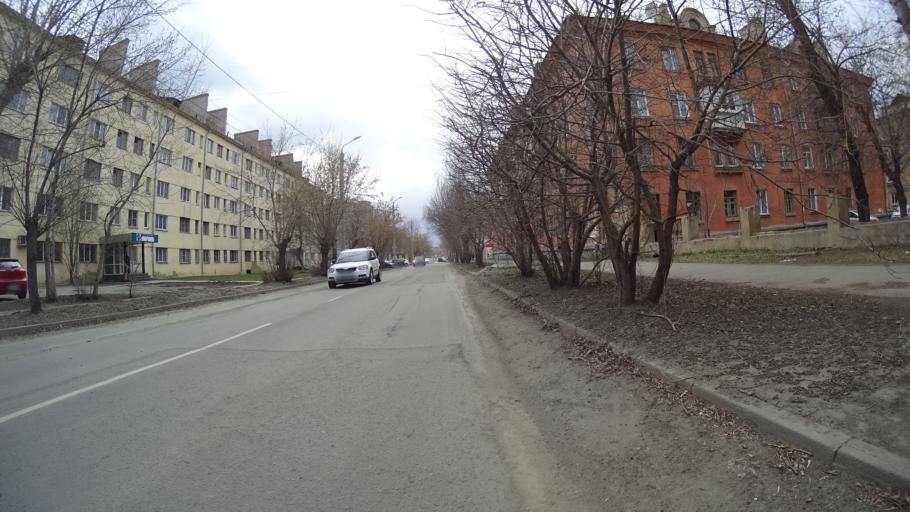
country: RU
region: Chelyabinsk
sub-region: Gorod Chelyabinsk
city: Chelyabinsk
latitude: 55.1622
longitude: 61.4402
